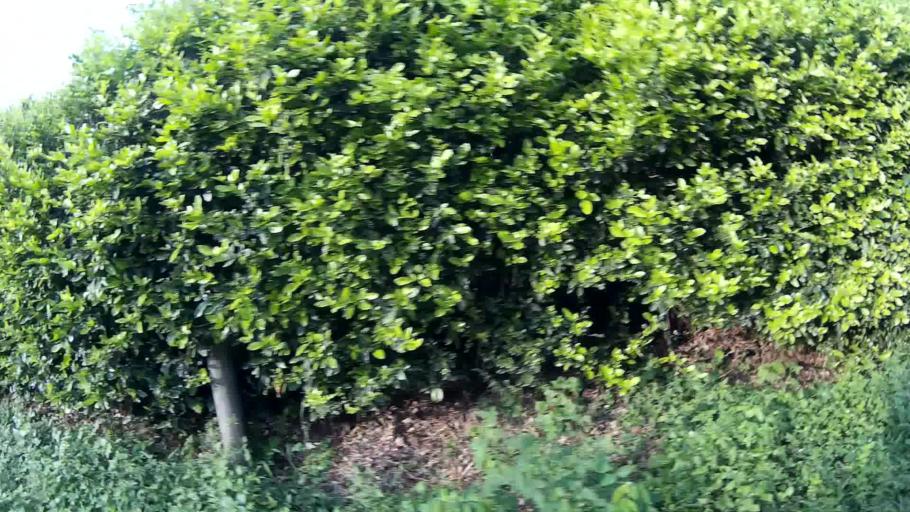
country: CO
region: Valle del Cauca
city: Ulloa
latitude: 4.7547
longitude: -75.7449
